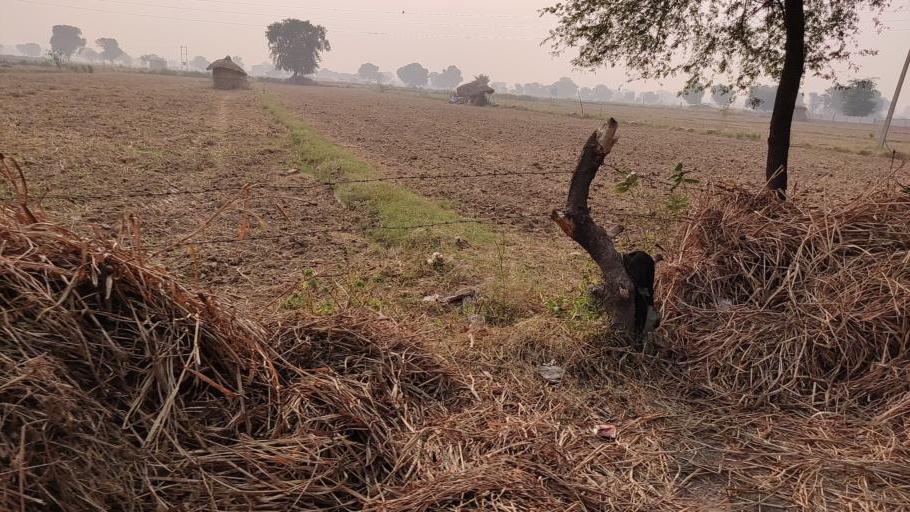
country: IN
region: Uttar Pradesh
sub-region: Mathura
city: Vrindavan
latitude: 27.5478
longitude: 77.7123
